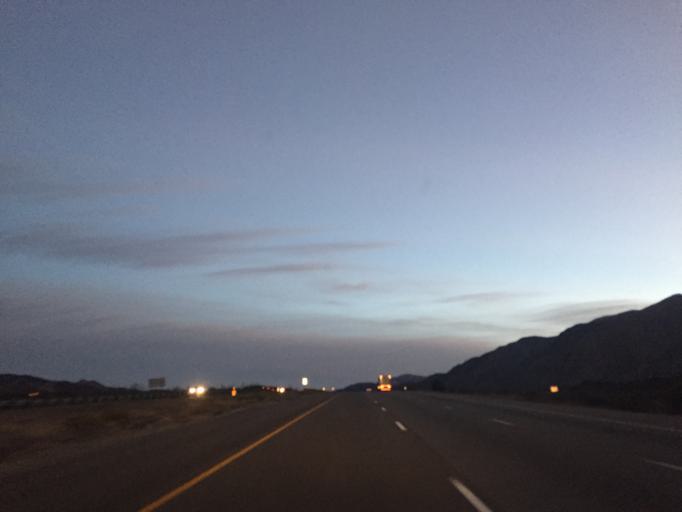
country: US
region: Utah
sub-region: Washington County
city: Toquerville
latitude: 37.3132
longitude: -113.2939
